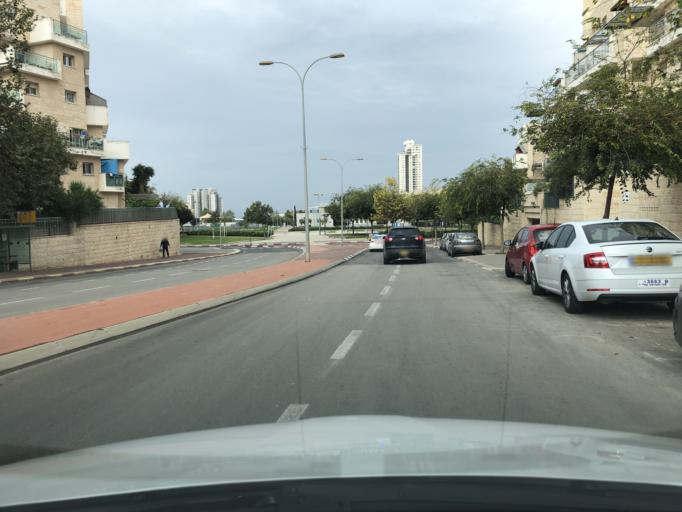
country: IL
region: Central District
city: Modiin
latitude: 31.9108
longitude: 35.0132
